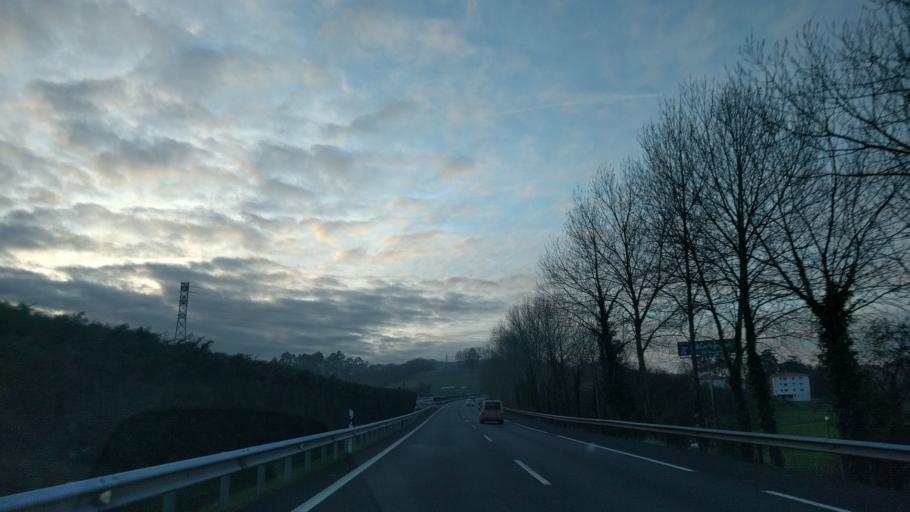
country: ES
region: Cantabria
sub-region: Provincia de Cantabria
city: Colindres
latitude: 43.3908
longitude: -3.4685
